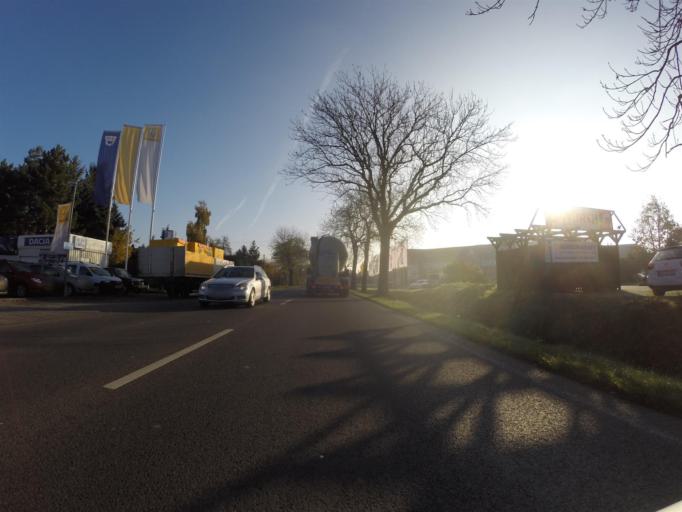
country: DE
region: Saxony
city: Markranstadt
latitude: 51.3453
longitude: 12.2730
